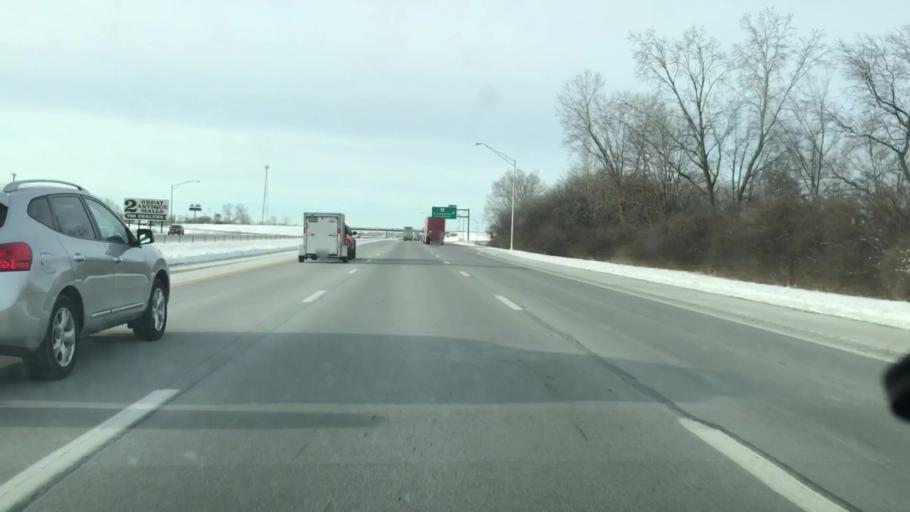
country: US
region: Ohio
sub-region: Clark County
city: Lisbon
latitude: 39.9001
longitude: -83.7178
